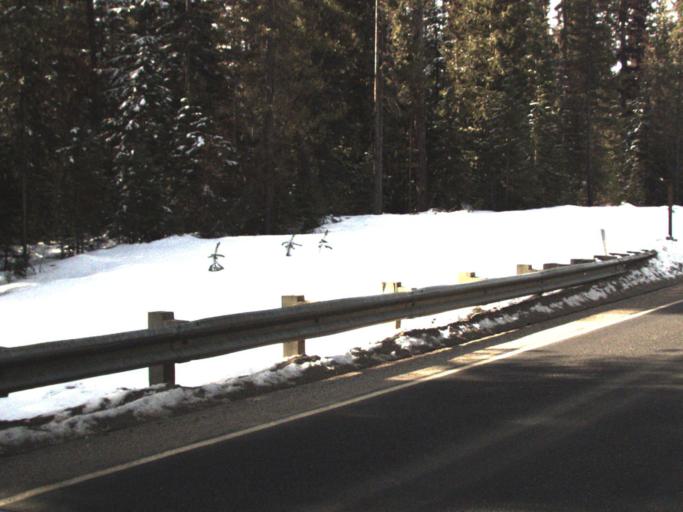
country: US
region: Washington
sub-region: Stevens County
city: Colville
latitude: 48.6385
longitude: -117.5305
